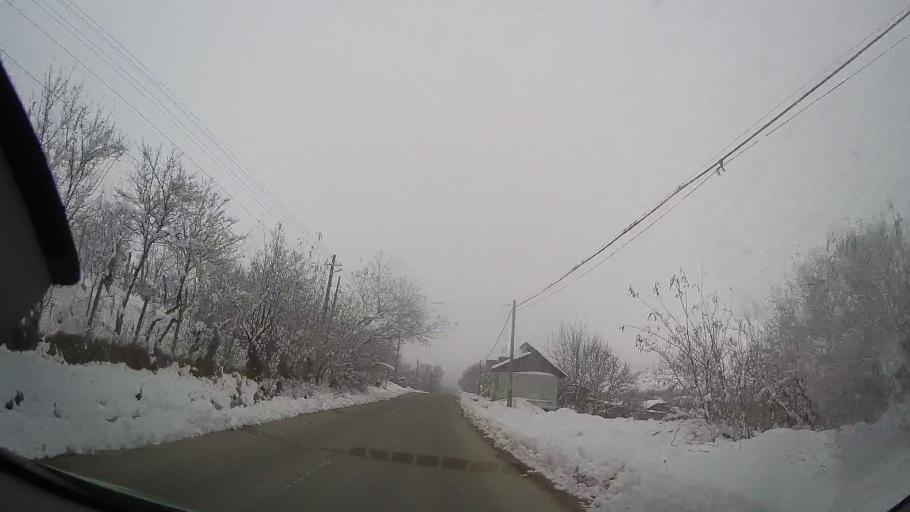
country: RO
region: Neamt
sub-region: Comuna Bozieni
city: Bozieni
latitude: 46.8421
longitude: 27.1460
